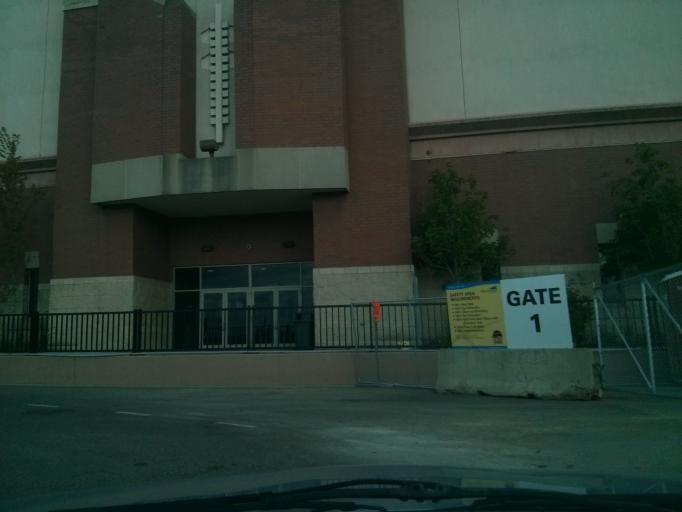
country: US
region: Minnesota
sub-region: Hennepin County
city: Richfield
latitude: 44.8562
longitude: -93.2406
